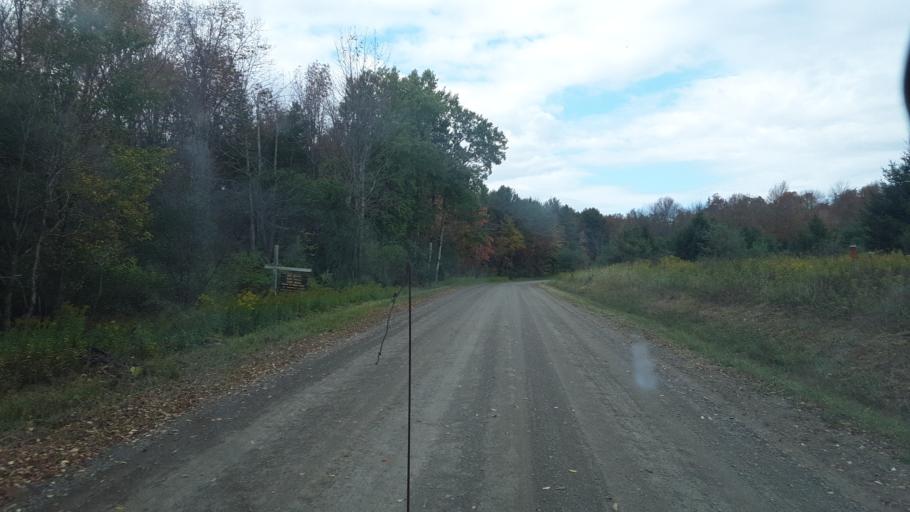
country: US
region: New York
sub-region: Allegany County
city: Alfred
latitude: 42.3872
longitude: -77.8651
